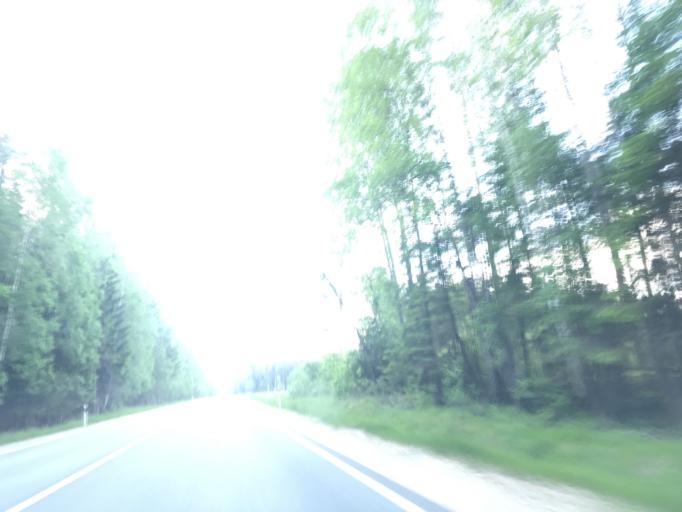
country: LV
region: Lielvarde
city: Lielvarde
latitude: 56.6724
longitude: 24.8601
